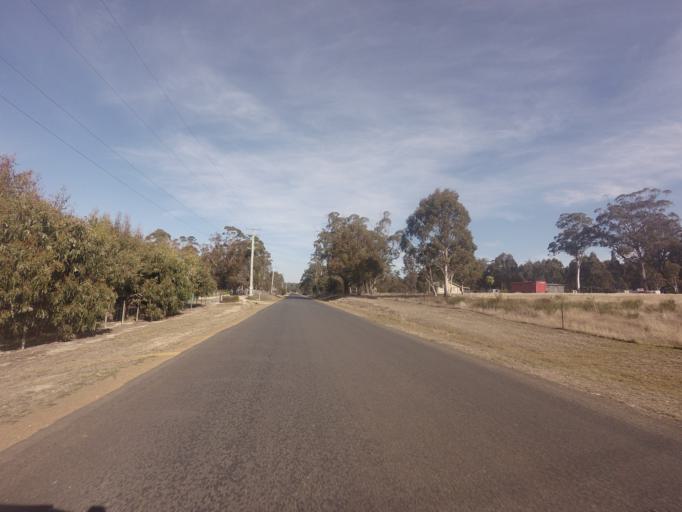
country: AU
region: Tasmania
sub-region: Sorell
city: Sorell
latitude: -42.4637
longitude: 147.4612
